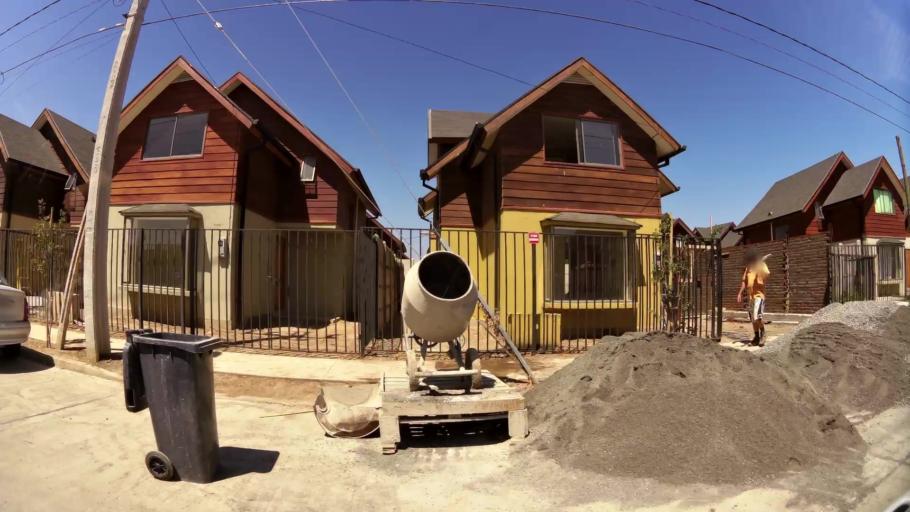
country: CL
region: Maule
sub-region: Provincia de Talca
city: Talca
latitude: -35.4265
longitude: -71.6165
